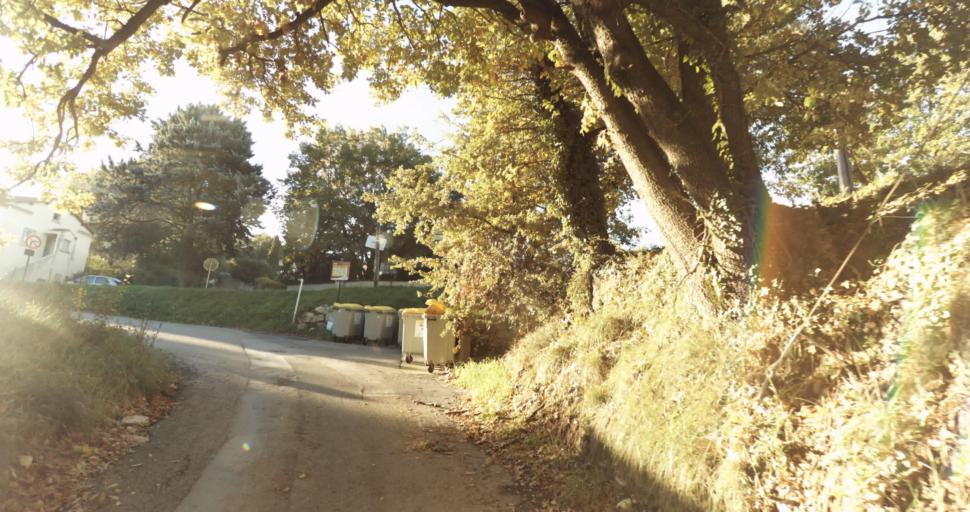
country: FR
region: Provence-Alpes-Cote d'Azur
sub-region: Departement des Bouches-du-Rhone
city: Venelles
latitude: 43.6027
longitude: 5.4794
